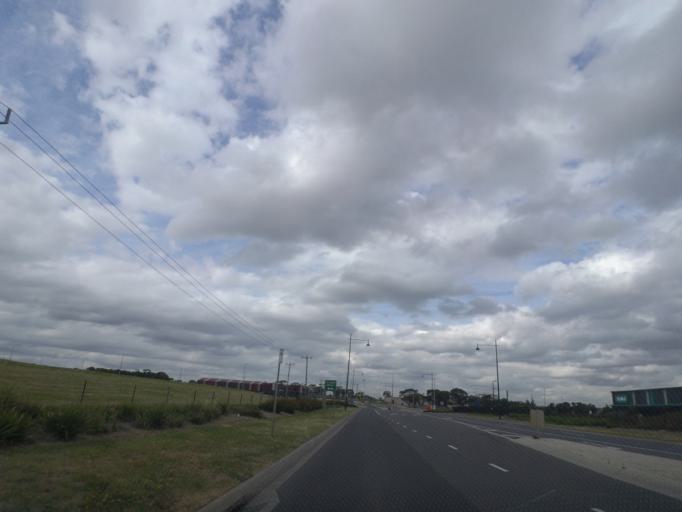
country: AU
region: Victoria
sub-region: Hume
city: Tullamarine
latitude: -37.6925
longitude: 144.8640
